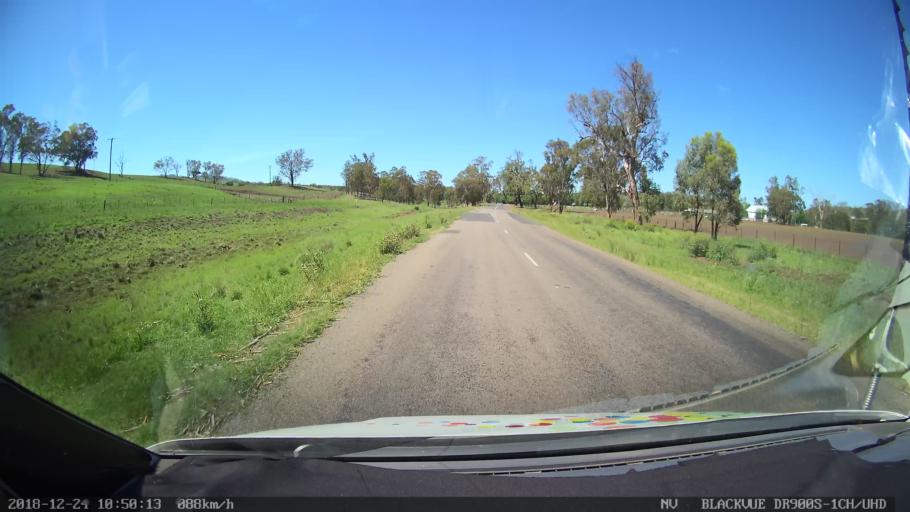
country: AU
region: New South Wales
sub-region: Upper Hunter Shire
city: Merriwa
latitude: -31.9574
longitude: 150.4244
